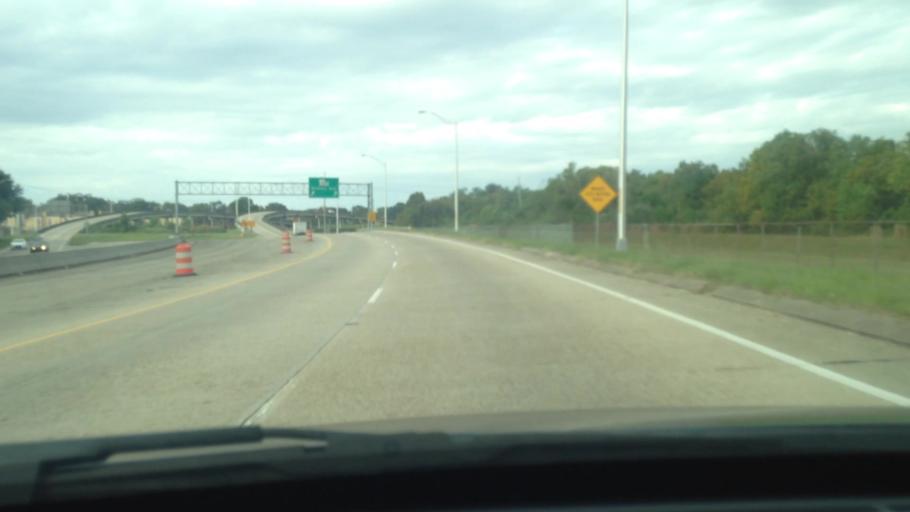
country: US
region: Louisiana
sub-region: Jefferson Parish
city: Elmwood
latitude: 29.9692
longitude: -90.1966
